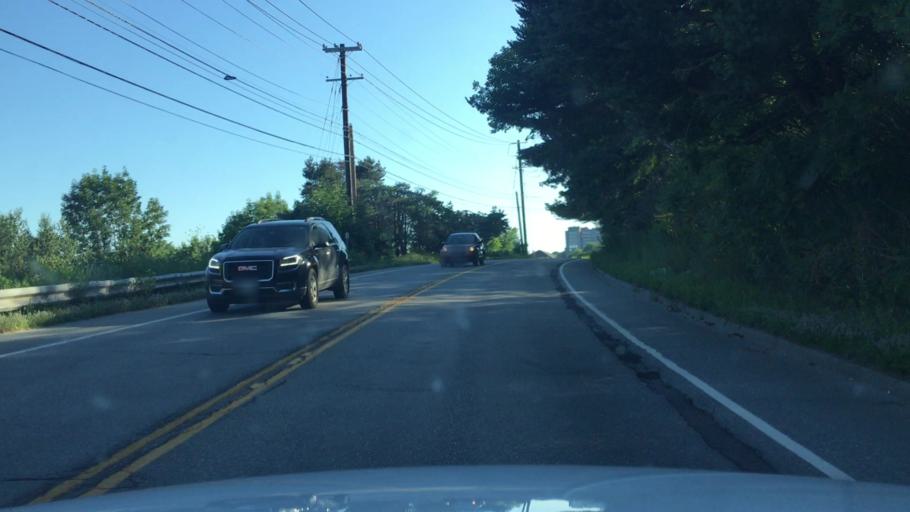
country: US
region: Maine
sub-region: Penobscot County
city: Brewer
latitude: 44.8129
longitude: -68.7399
